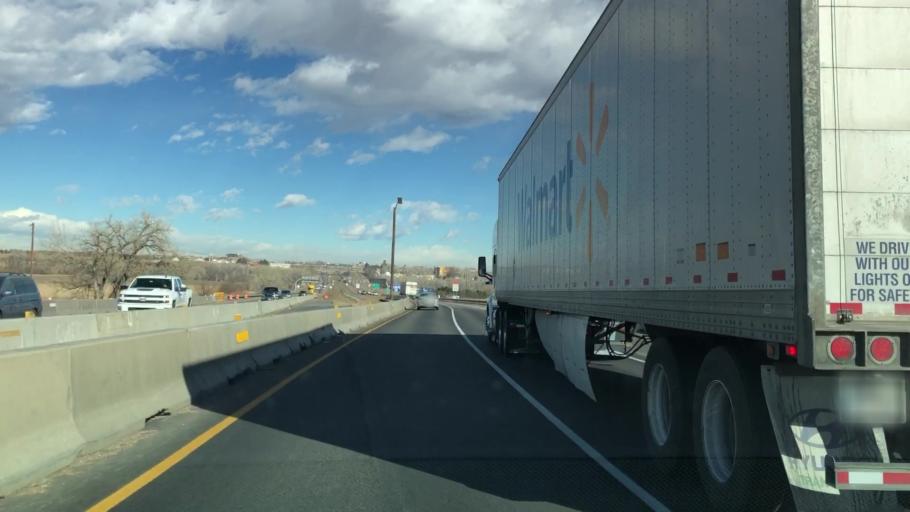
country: US
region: Colorado
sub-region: Larimer County
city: Loveland
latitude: 40.3850
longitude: -104.9893
